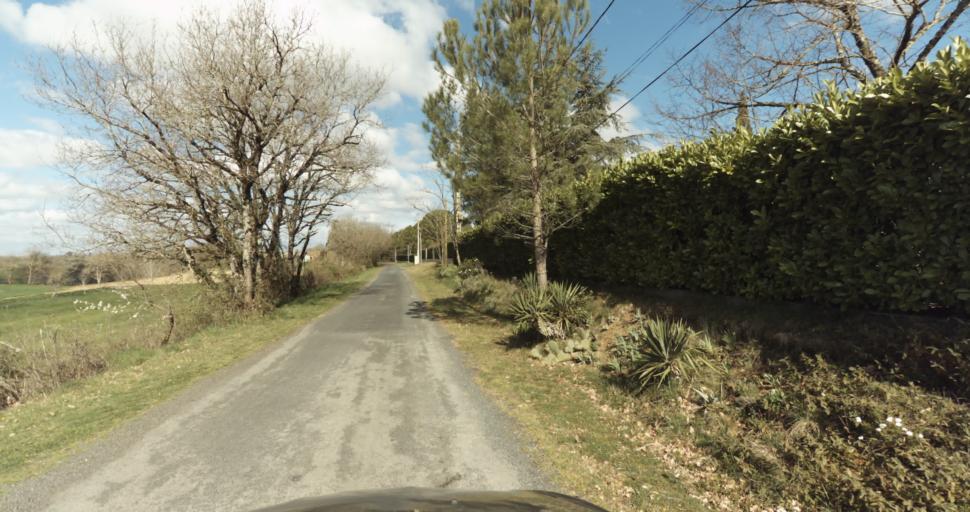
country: FR
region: Midi-Pyrenees
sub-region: Departement du Tarn
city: Puygouzon
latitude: 43.8670
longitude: 2.1738
